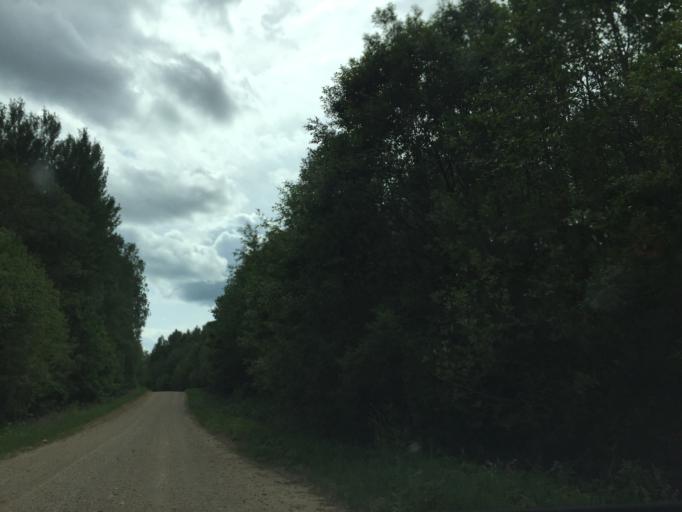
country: LV
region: Dagda
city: Dagda
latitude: 56.0490
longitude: 27.6434
